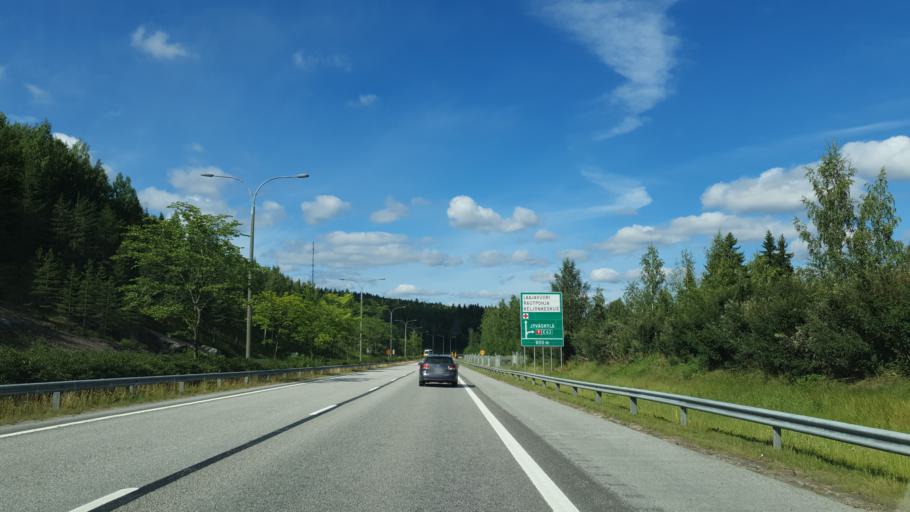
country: FI
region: Central Finland
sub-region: Jyvaeskylae
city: Jyvaeskylae
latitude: 62.2007
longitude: 25.7098
